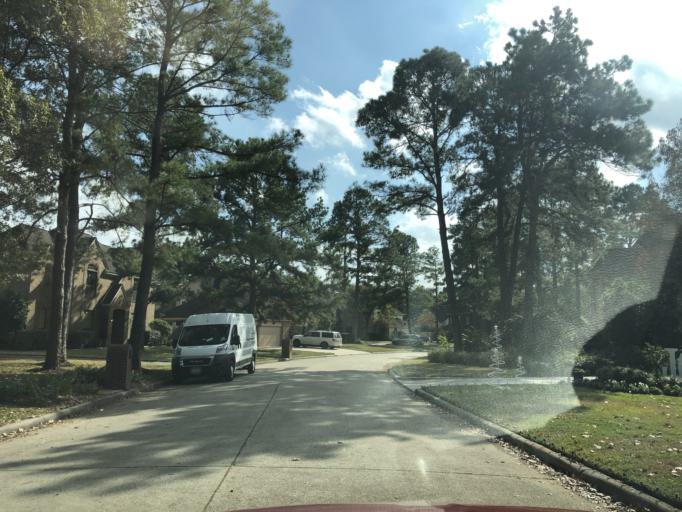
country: US
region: Texas
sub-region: Harris County
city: Tomball
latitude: 30.0232
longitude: -95.5458
